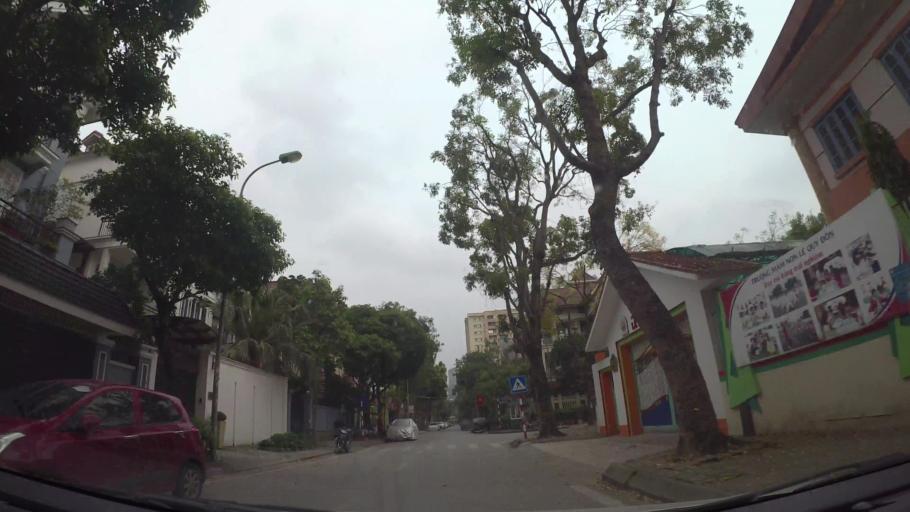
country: VN
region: Ha Noi
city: Cau Dien
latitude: 21.0327
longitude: 105.7673
